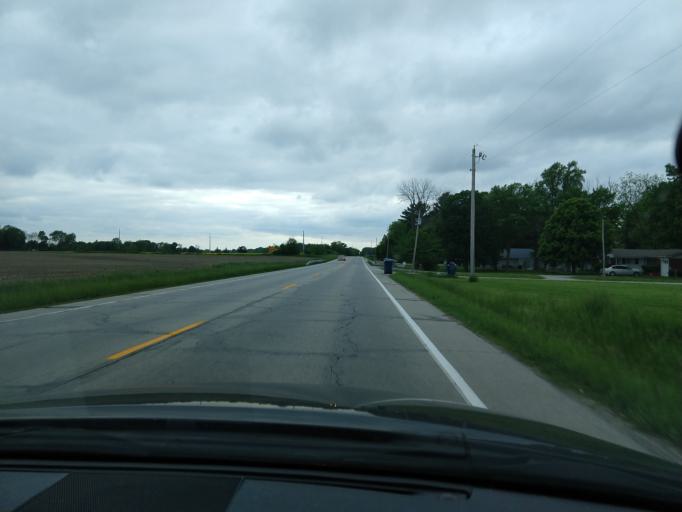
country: US
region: Indiana
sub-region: Madison County
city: Lapel
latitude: 40.0536
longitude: -85.9221
